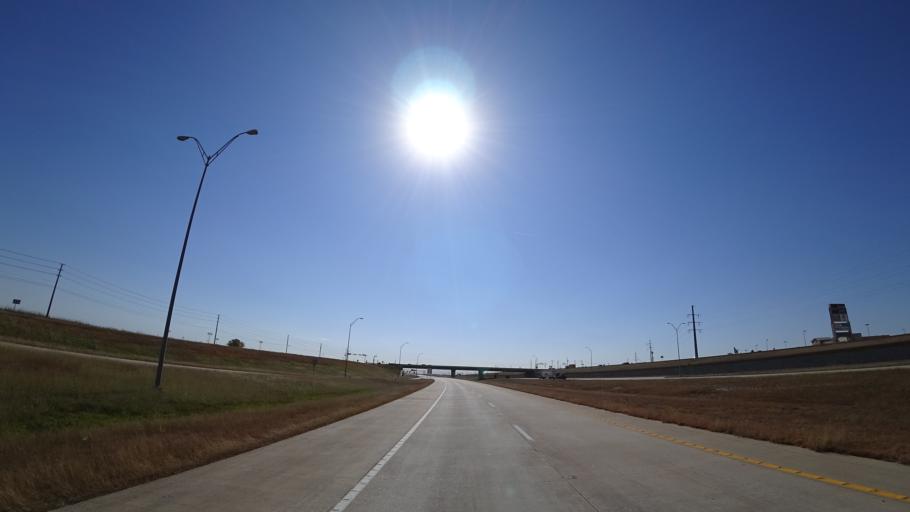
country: US
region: Texas
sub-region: Travis County
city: Pflugerville
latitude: 30.4674
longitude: -97.5940
